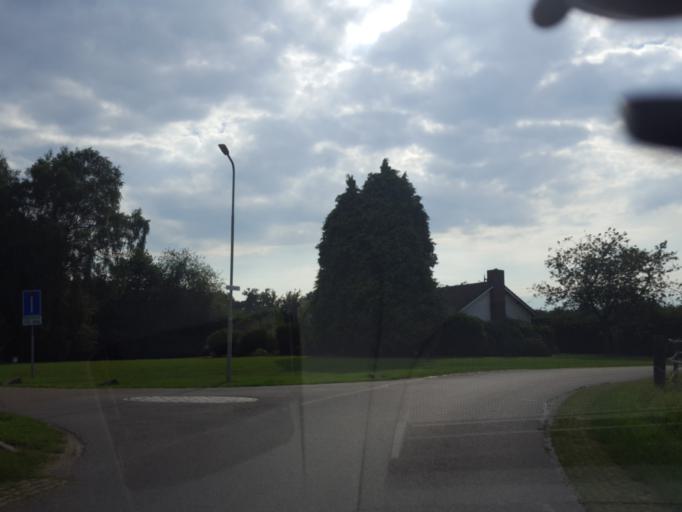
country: NL
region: Limburg
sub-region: Gemeente Bergen
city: Wellerlooi
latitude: 51.5211
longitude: 6.0909
